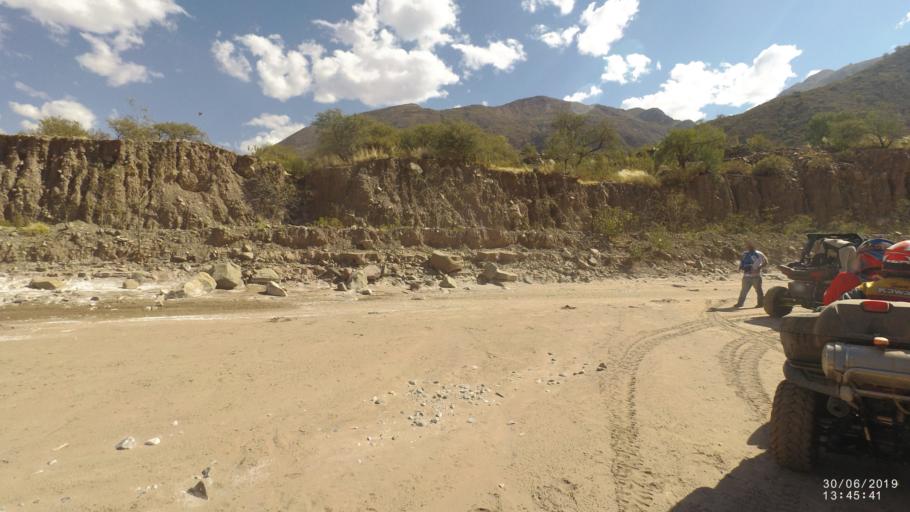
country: BO
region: Cochabamba
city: Irpa Irpa
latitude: -17.8076
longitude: -66.3586
